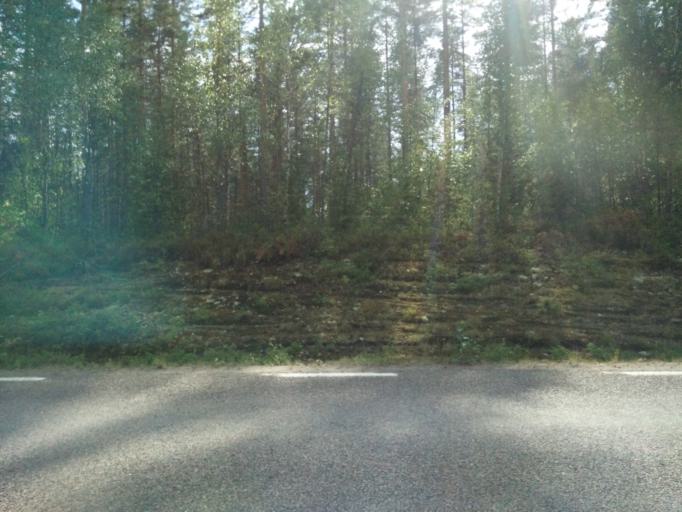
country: SE
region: Vaermland
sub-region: Munkfors Kommun
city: Munkfors
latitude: 59.9679
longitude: 13.5459
